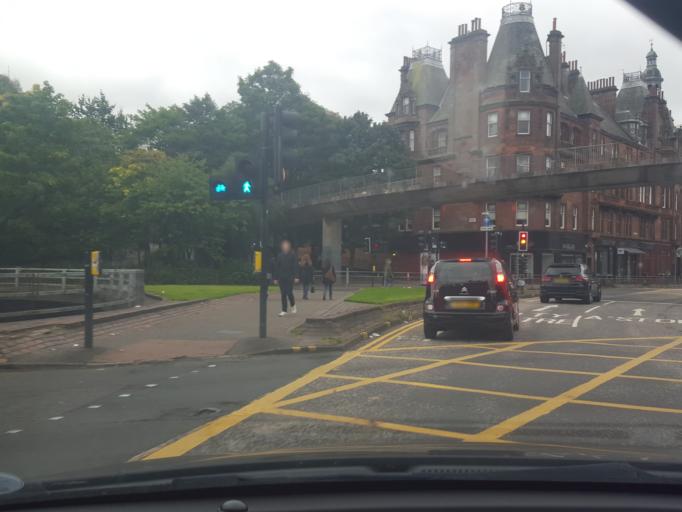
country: GB
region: Scotland
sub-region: Glasgow City
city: Glasgow
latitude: 55.8675
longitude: -4.2712
